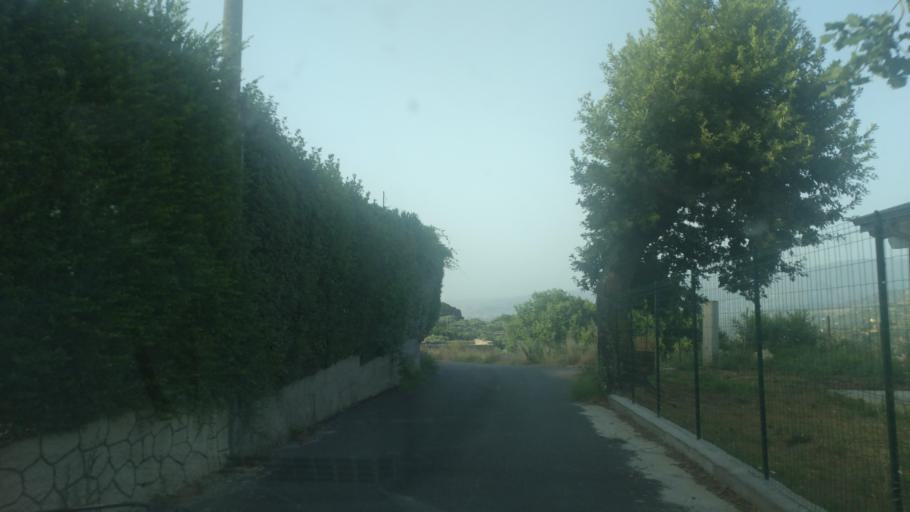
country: IT
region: Calabria
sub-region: Provincia di Catanzaro
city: Staletti
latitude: 38.7642
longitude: 16.5326
